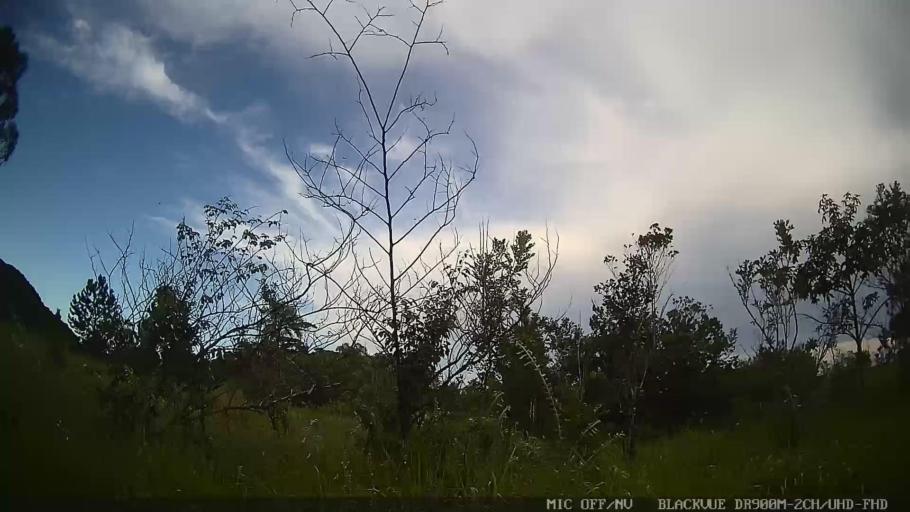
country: BR
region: Sao Paulo
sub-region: Iguape
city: Iguape
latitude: -24.6889
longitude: -47.5191
